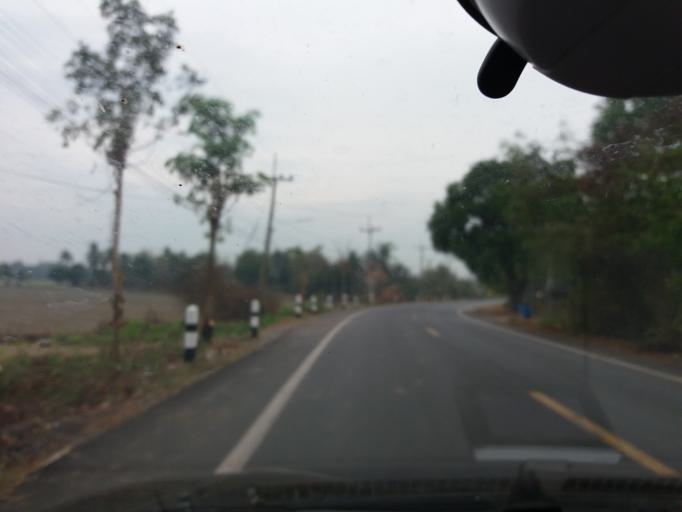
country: TH
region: Suphan Buri
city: Doembang Nangbuat
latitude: 14.8327
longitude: 100.1164
